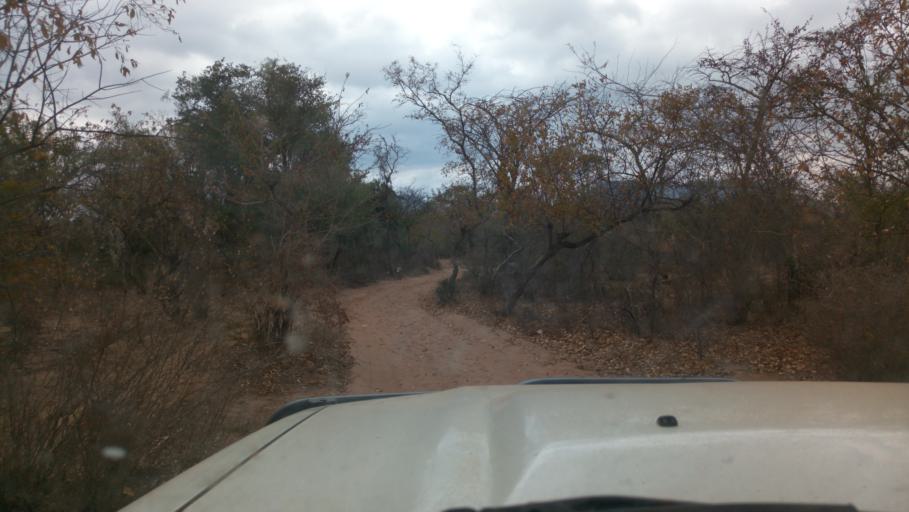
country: KE
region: Kitui
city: Kitui
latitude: -1.8456
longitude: 38.3542
